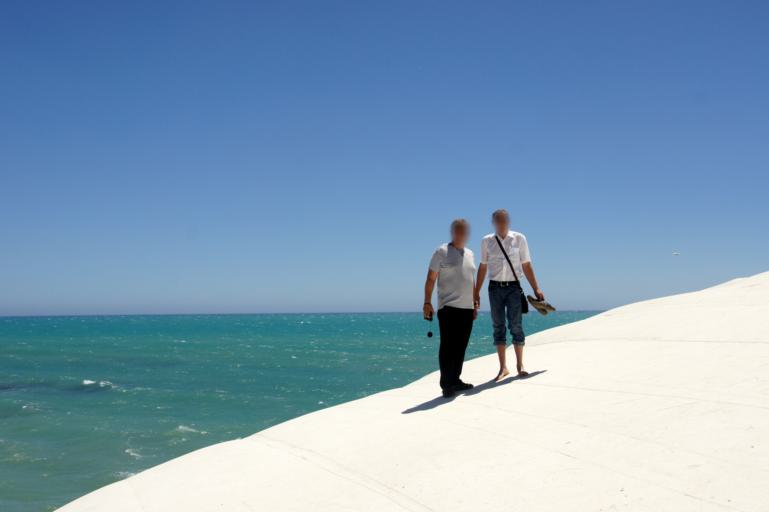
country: IT
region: Sicily
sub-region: Agrigento
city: Realmonte
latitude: 37.2897
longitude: 13.4726
